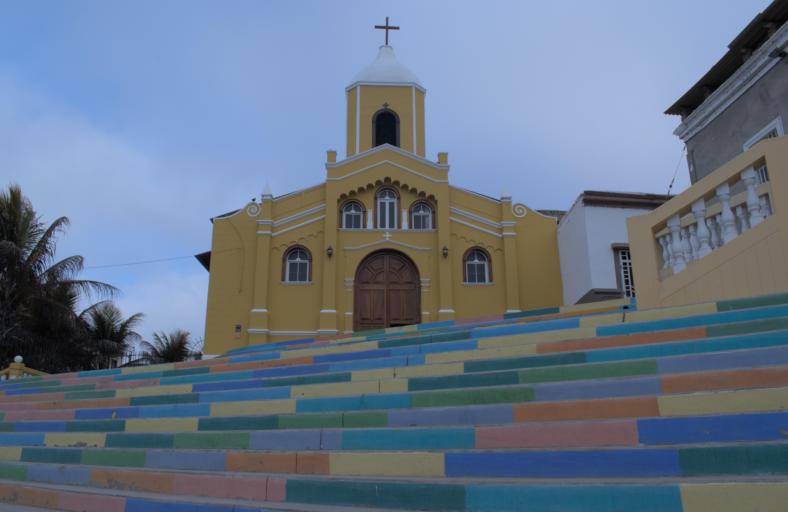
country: PE
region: La Libertad
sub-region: Provincia de Pacasmayo
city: Pacasmayo
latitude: -7.3998
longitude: -79.5719
